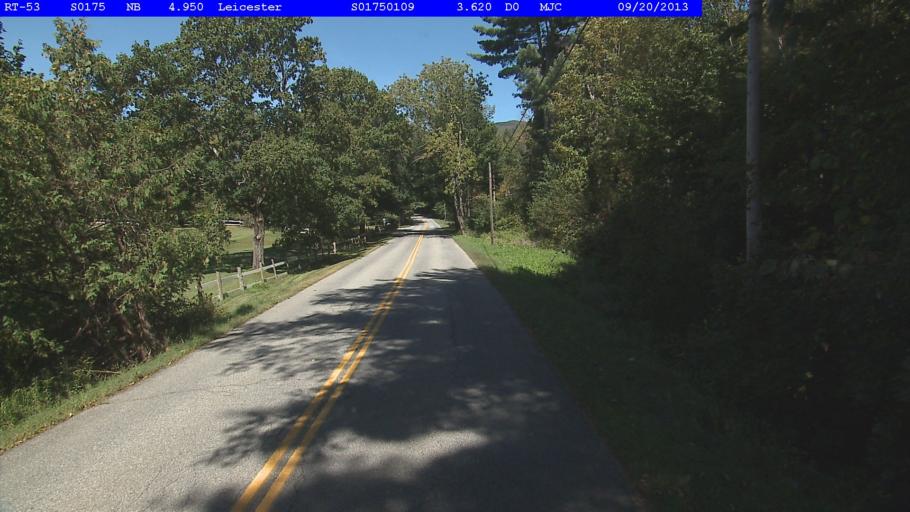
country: US
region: Vermont
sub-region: Rutland County
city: Brandon
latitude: 43.8947
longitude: -73.0644
